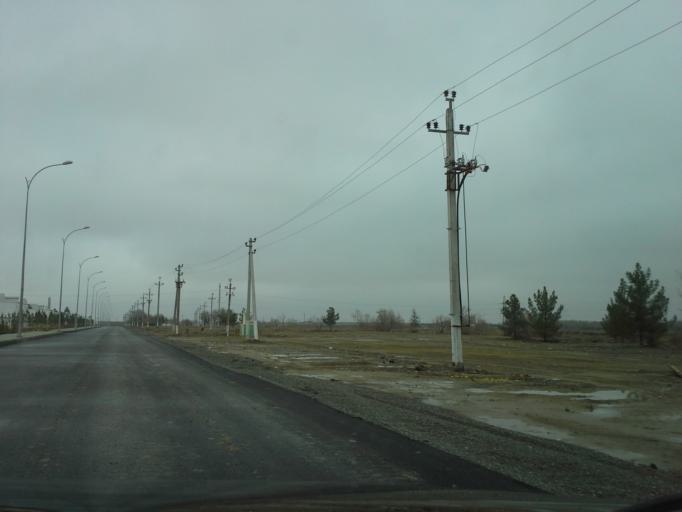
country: TM
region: Ahal
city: Ashgabat
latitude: 37.9704
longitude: 58.4069
